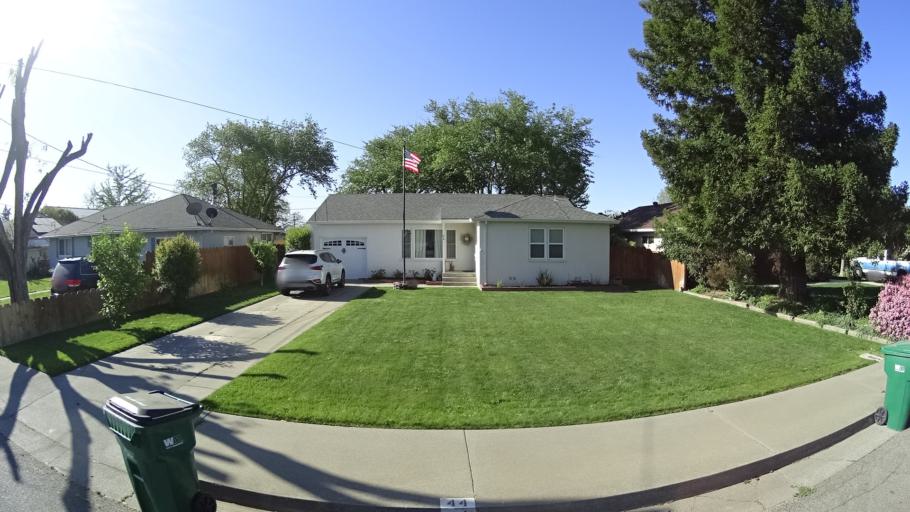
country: US
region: California
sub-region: Glenn County
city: Orland
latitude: 39.7426
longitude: -122.1860
